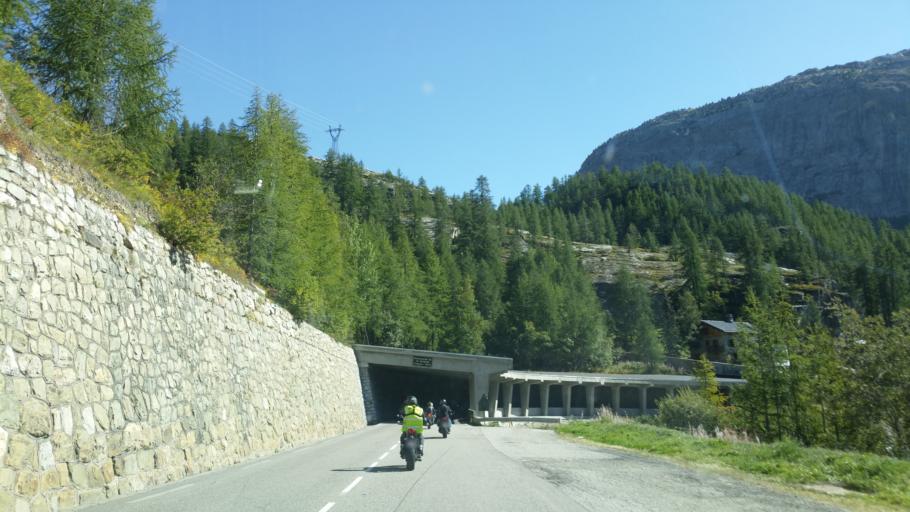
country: FR
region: Rhone-Alpes
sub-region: Departement de la Savoie
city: Tignes
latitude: 45.4781
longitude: 6.9497
